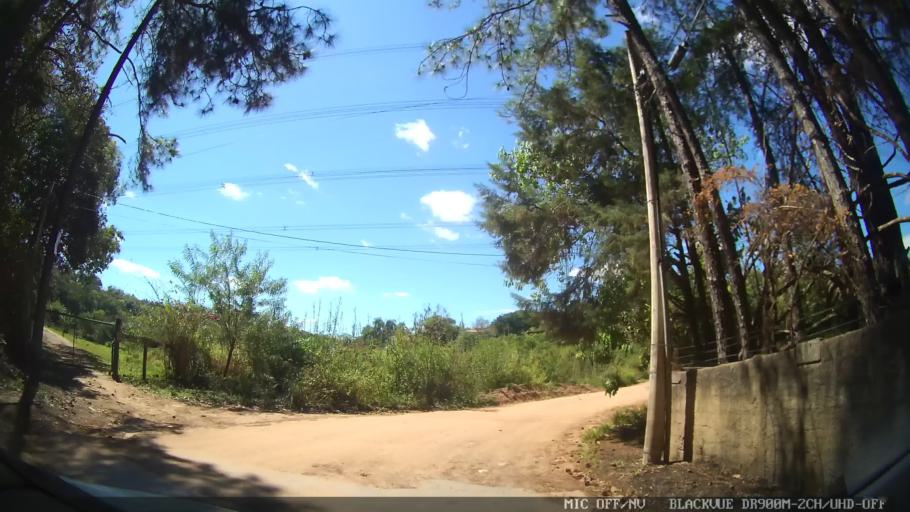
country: BR
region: Sao Paulo
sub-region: Jarinu
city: Jarinu
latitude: -23.1570
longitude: -46.7166
